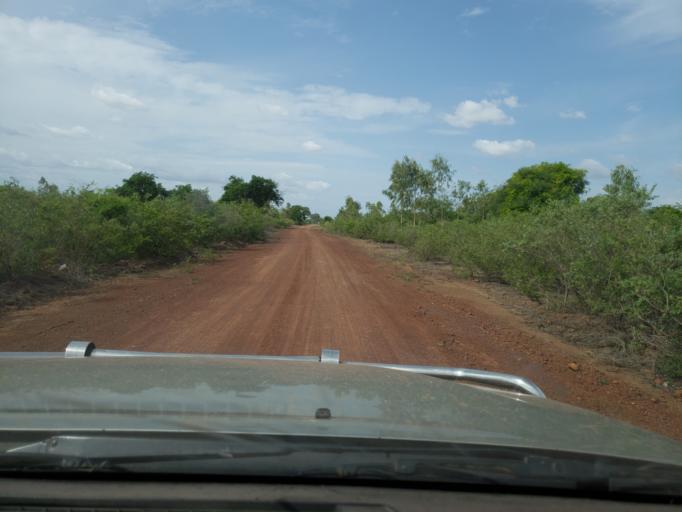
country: ML
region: Segou
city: Bla
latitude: 12.7614
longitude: -5.6241
